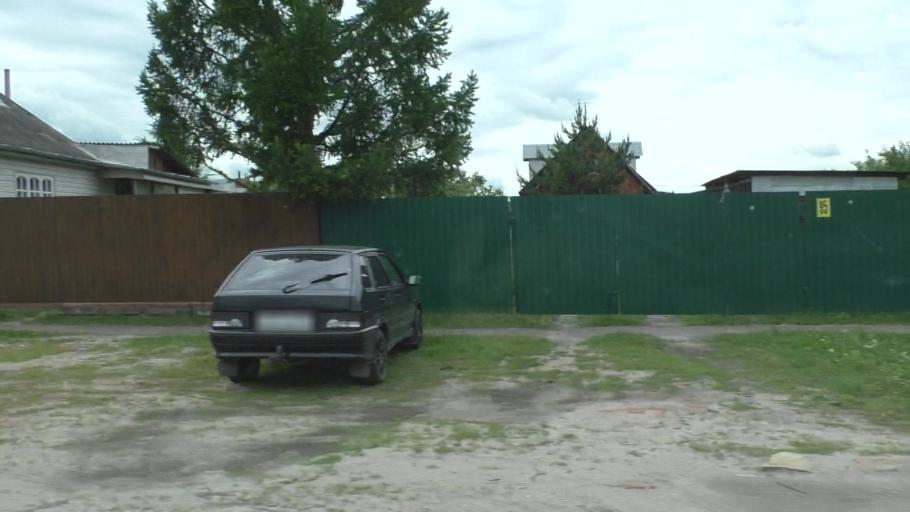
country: RU
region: Moskovskaya
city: Il'inskiy Pogost
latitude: 55.5036
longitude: 38.7865
